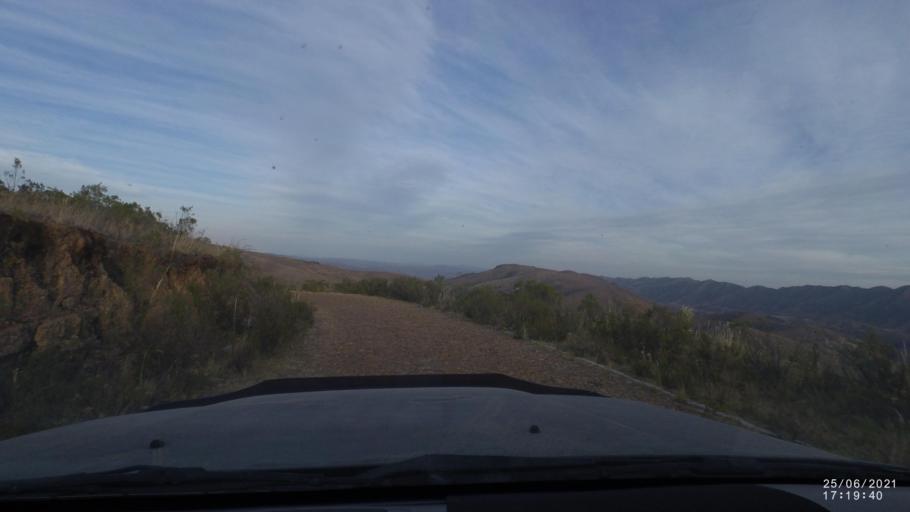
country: BO
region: Cochabamba
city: Arani
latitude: -17.9042
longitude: -65.6934
